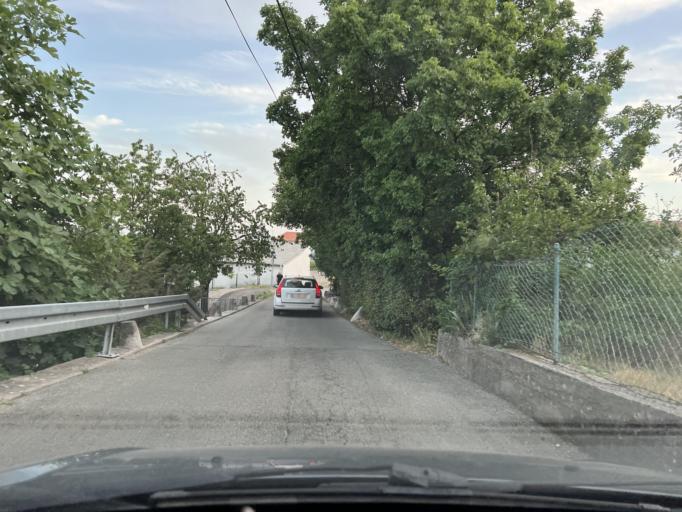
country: HR
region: Primorsko-Goranska
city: Marcelji
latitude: 45.3894
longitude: 14.4101
